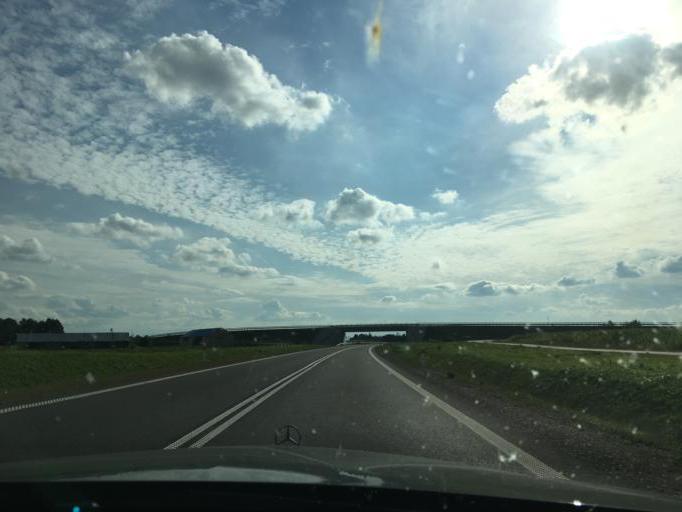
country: PL
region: Podlasie
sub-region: Powiat grajewski
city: Rajgrod
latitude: 53.7671
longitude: 22.8318
